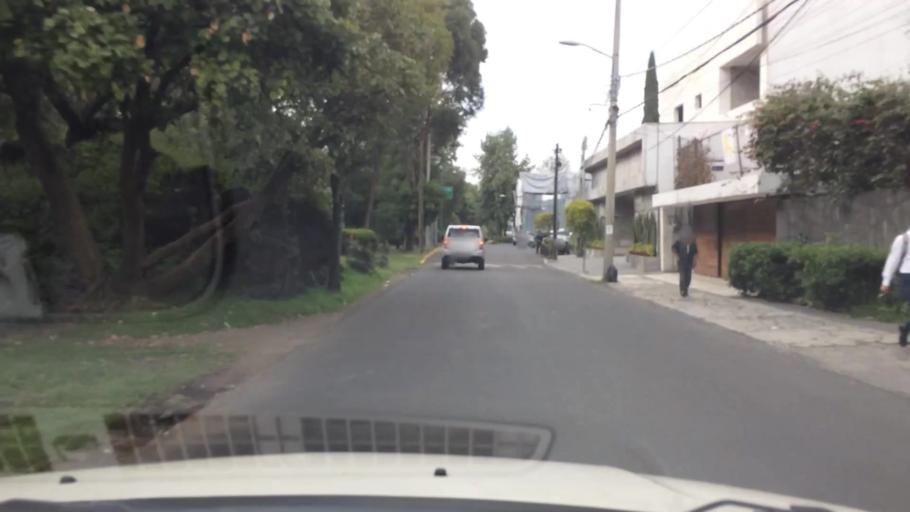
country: MX
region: Mexico City
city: Magdalena Contreras
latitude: 19.3147
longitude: -99.2122
